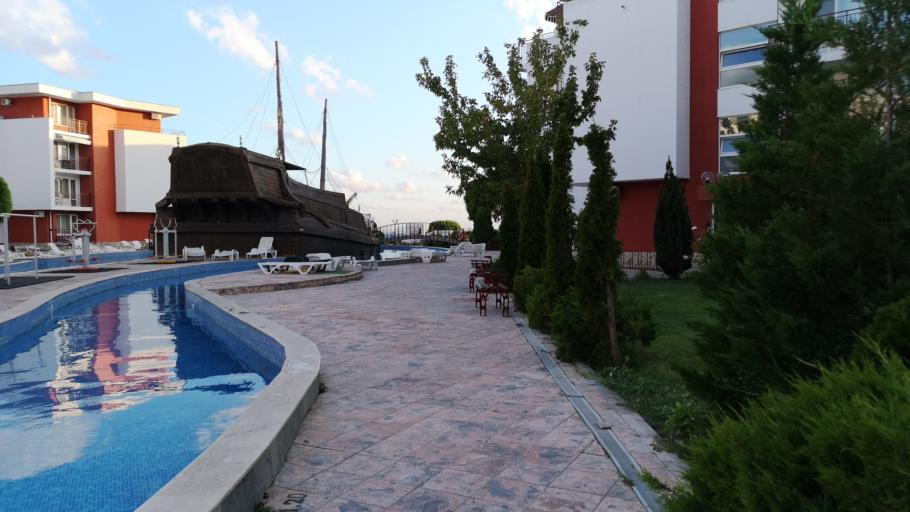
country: BG
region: Burgas
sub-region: Obshtina Nesebur
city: Sveti Vlas
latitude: 42.7024
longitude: 27.8077
